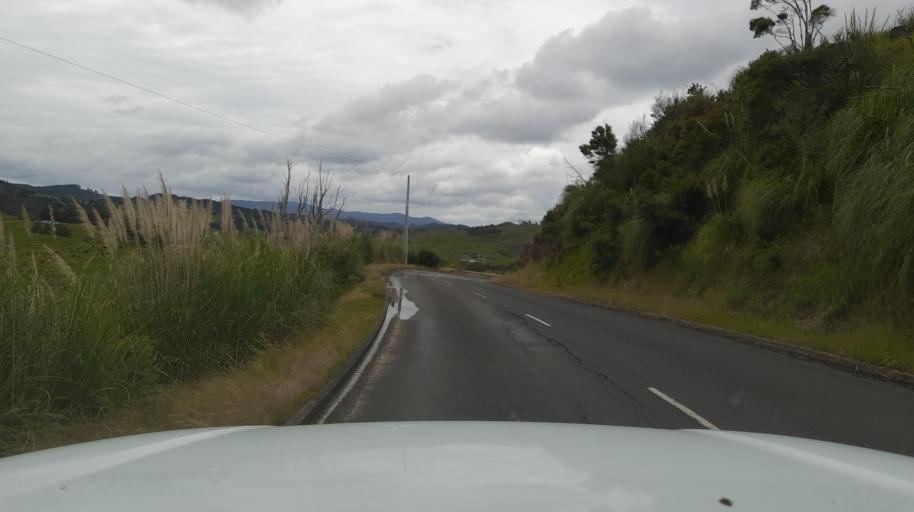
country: NZ
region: Northland
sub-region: Far North District
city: Kaitaia
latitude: -35.3676
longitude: 173.4324
